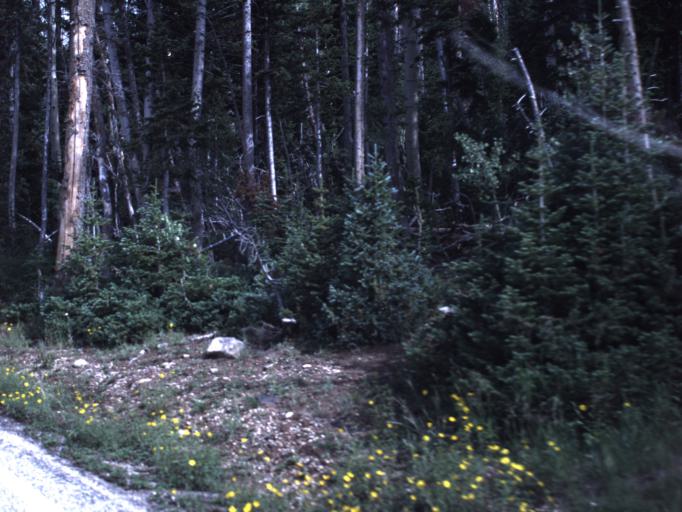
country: US
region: Utah
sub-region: Iron County
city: Cedar City
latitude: 37.5753
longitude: -112.8389
